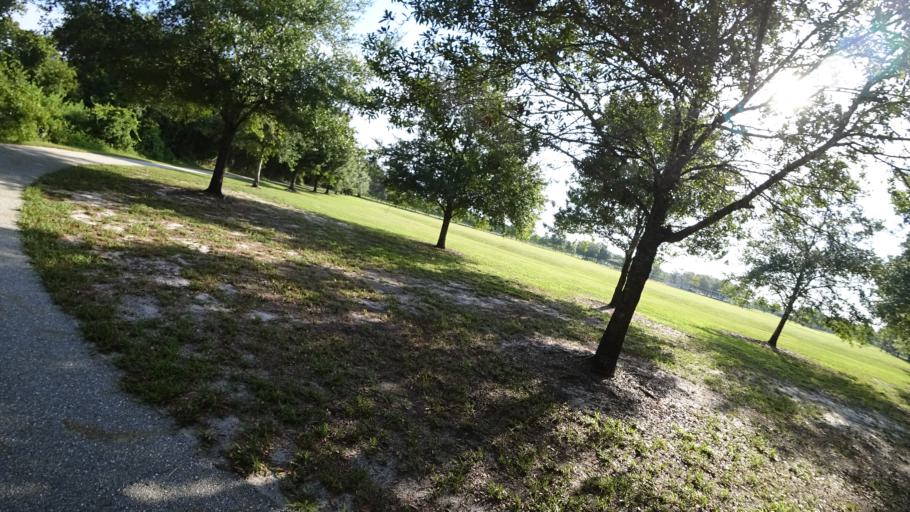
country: US
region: Florida
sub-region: Sarasota County
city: Lake Sarasota
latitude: 27.3579
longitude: -82.1658
